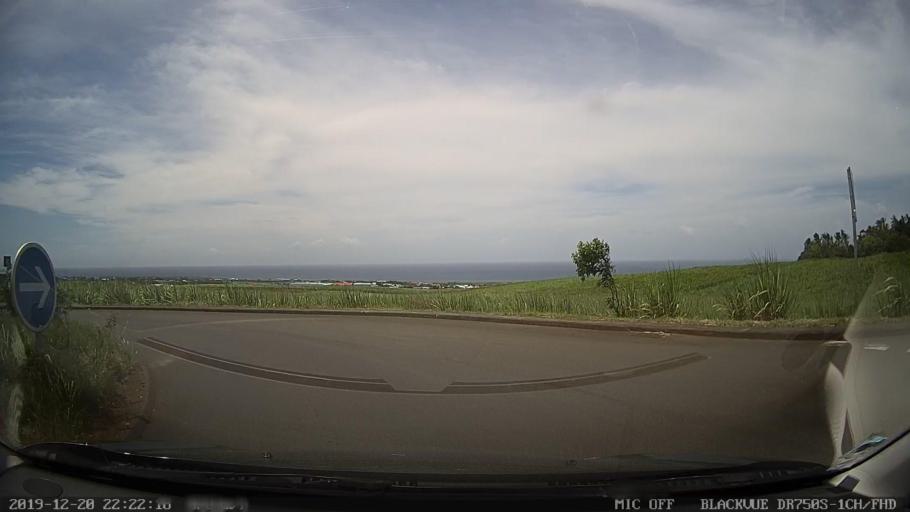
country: RE
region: Reunion
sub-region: Reunion
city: Sainte-Marie
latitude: -20.9161
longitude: 55.5242
